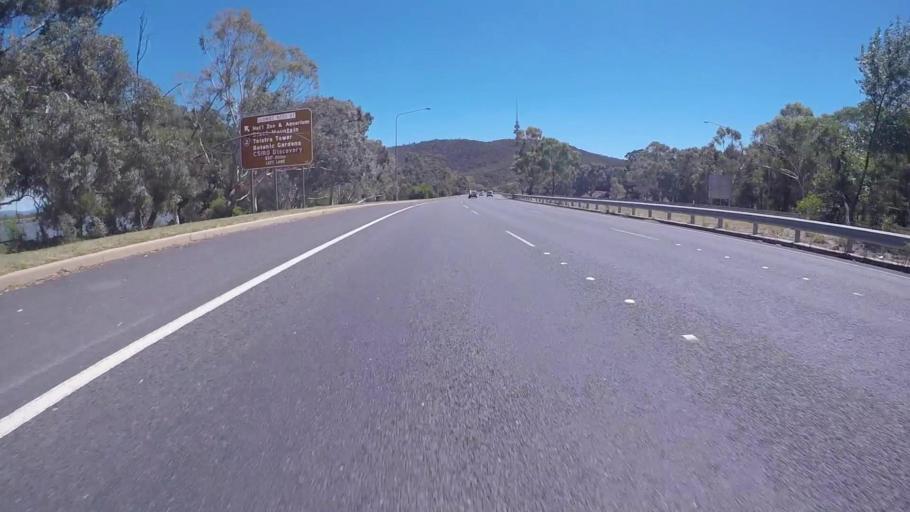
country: AU
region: Australian Capital Territory
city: Acton
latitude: -35.2862
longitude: 149.1138
